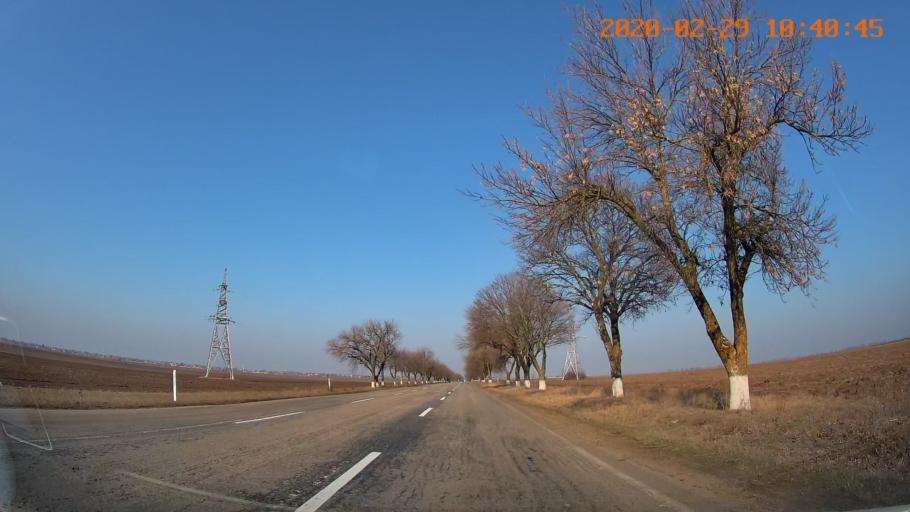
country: MD
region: Anenii Noi
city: Varnita
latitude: 47.0359
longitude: 29.4353
